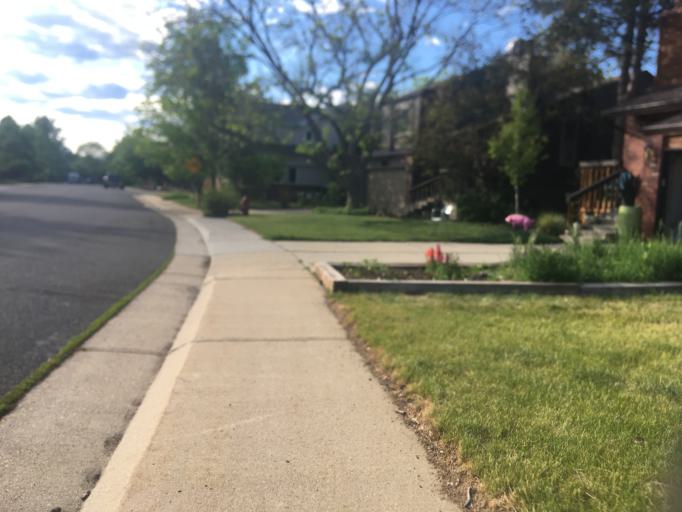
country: US
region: Colorado
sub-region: Boulder County
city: Louisville
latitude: 39.9880
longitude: -105.1588
